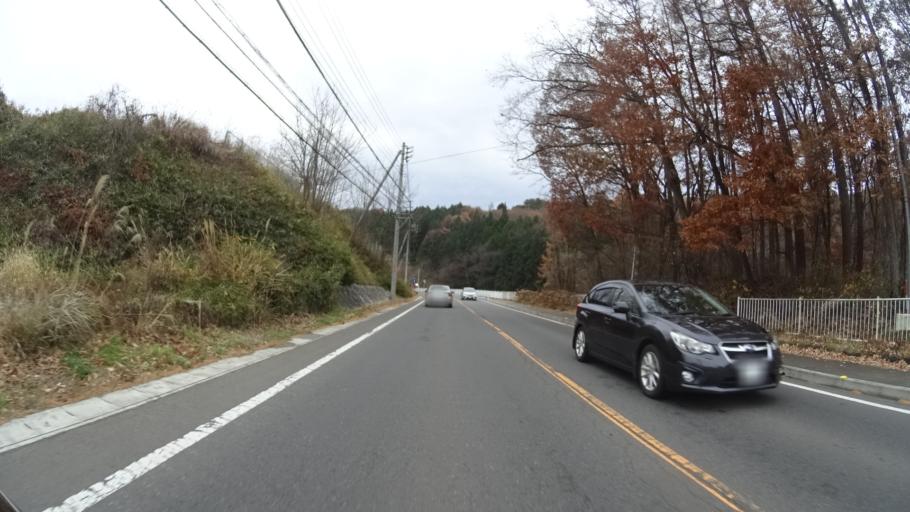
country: JP
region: Gunma
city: Numata
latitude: 36.6699
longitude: 139.1923
